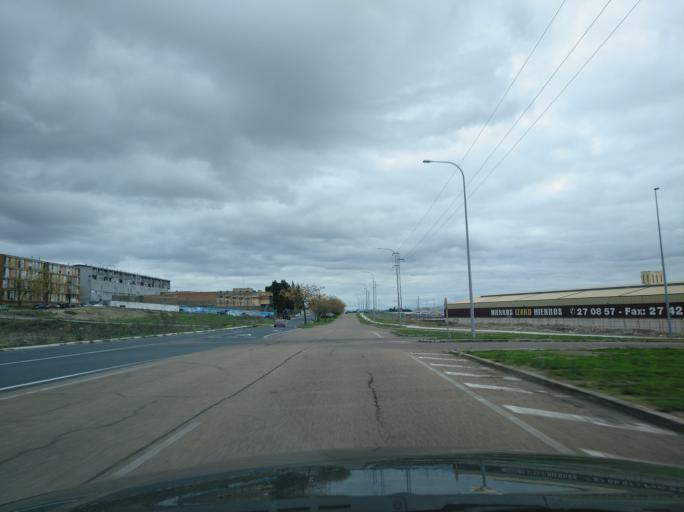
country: ES
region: Extremadura
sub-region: Provincia de Badajoz
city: Badajoz
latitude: 38.8982
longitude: -6.9862
